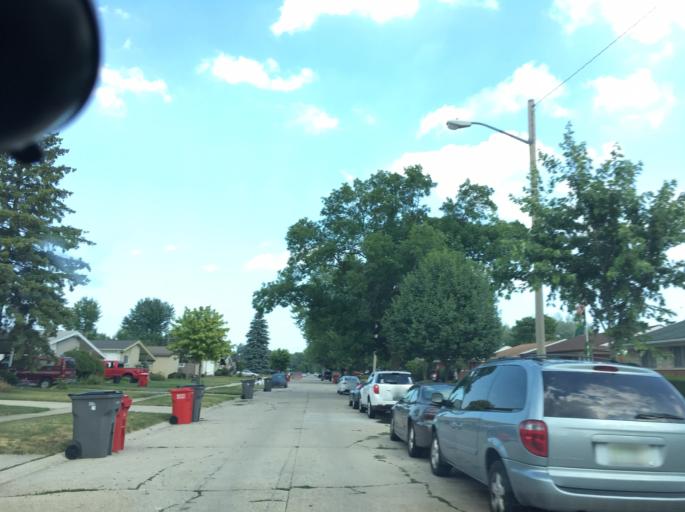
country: US
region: Michigan
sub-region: Macomb County
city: Fraser
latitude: 42.5489
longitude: -82.9184
